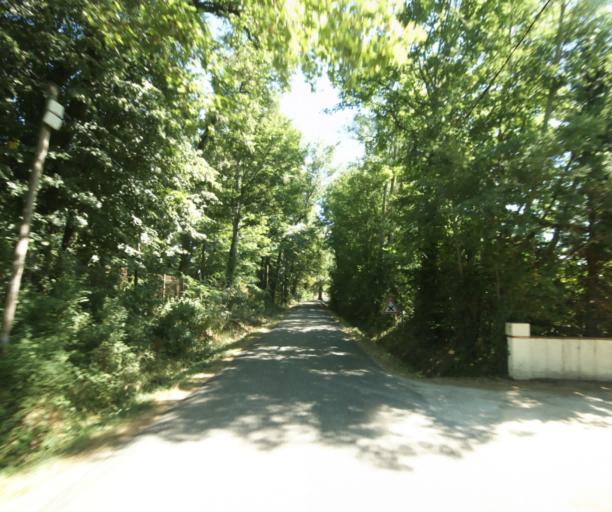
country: FR
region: Midi-Pyrenees
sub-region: Departement de la Haute-Garonne
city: Saint-Felix-Lauragais
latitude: 43.5115
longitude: 1.8897
